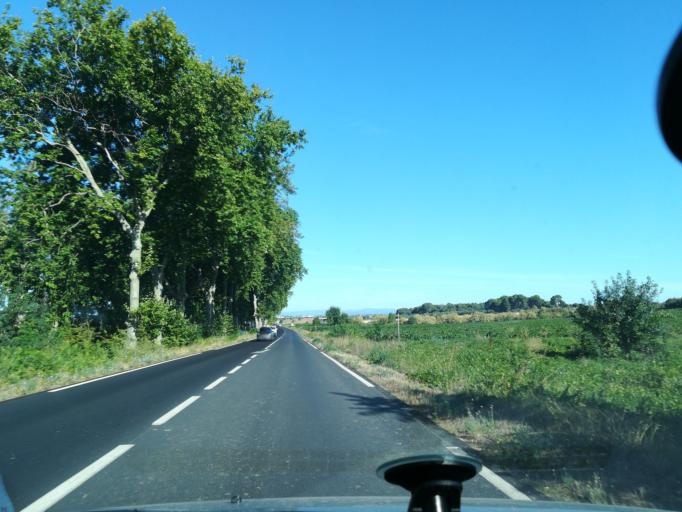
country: FR
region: Languedoc-Roussillon
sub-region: Departement de l'Herault
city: Portiragnes
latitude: 43.3081
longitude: 3.3246
